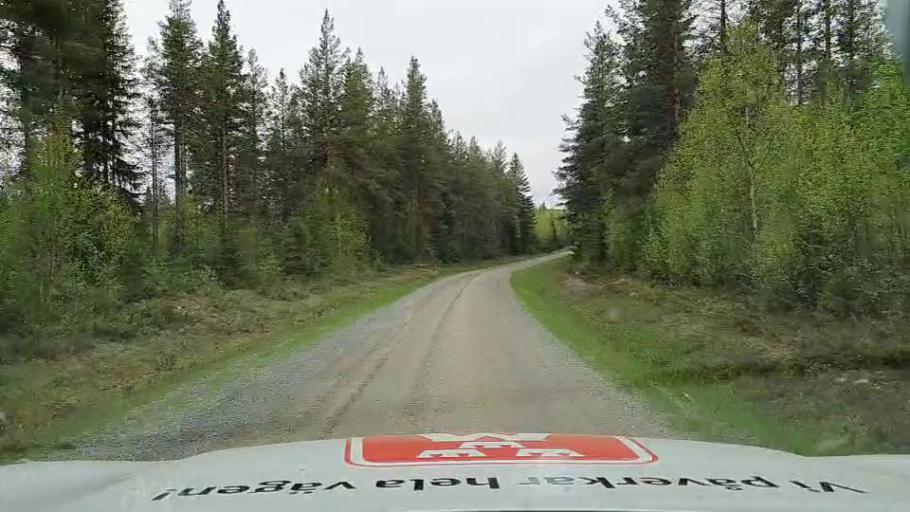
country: SE
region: Jaemtland
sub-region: Bergs Kommun
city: Hoverberg
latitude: 62.5140
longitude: 14.7068
